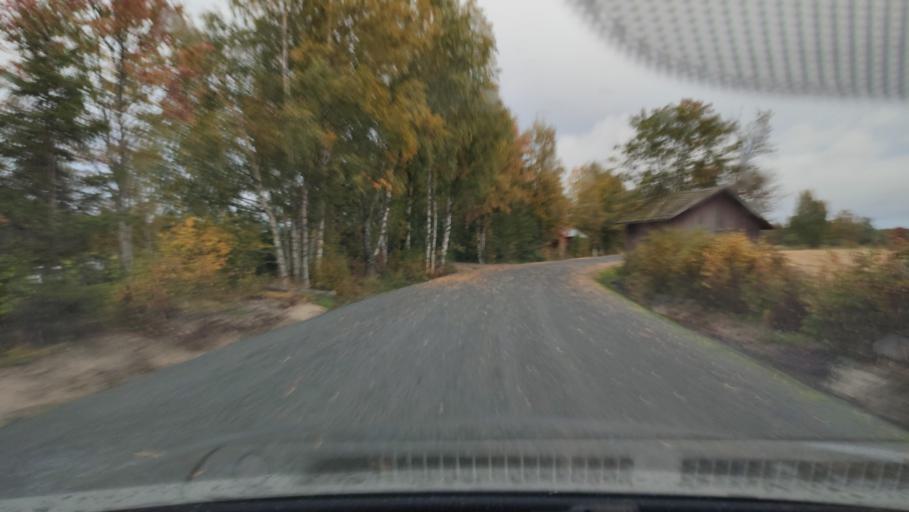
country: FI
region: Southern Ostrobothnia
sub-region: Suupohja
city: Karijoki
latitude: 62.2278
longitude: 21.6229
